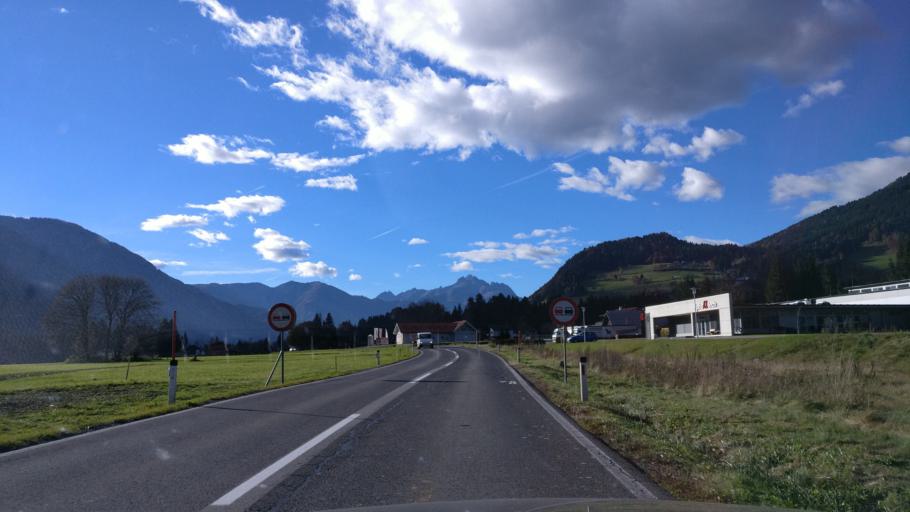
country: AT
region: Carinthia
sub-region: Politischer Bezirk Spittal an der Drau
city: Dellach im Drautal
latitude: 46.7384
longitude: 13.0950
